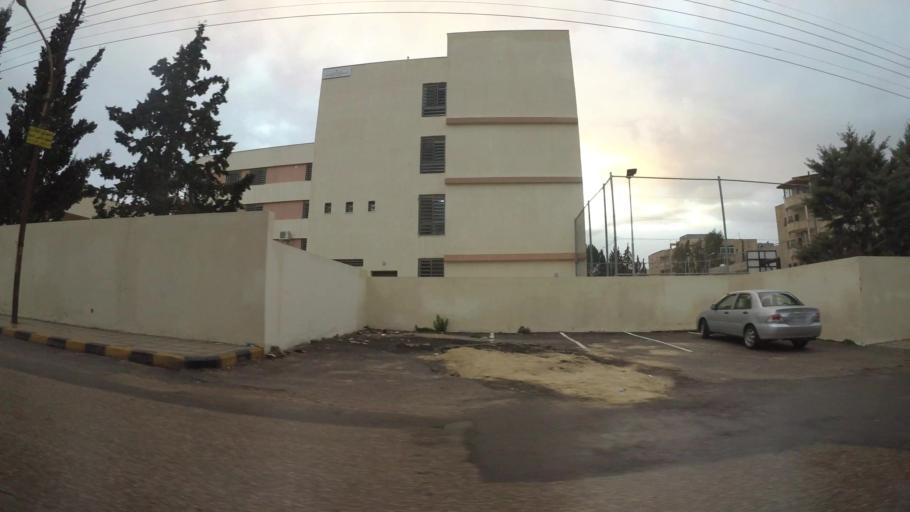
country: JO
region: Amman
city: Al Jubayhah
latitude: 32.0314
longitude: 35.8251
